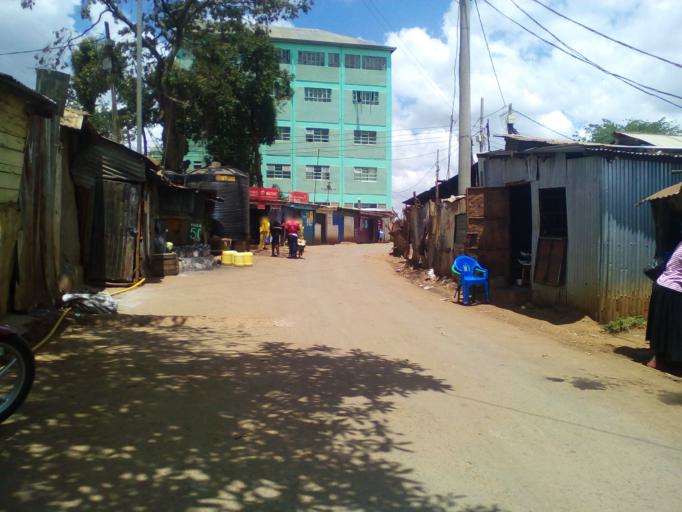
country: KE
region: Nairobi Area
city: Nairobi
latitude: -1.3106
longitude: 36.7858
